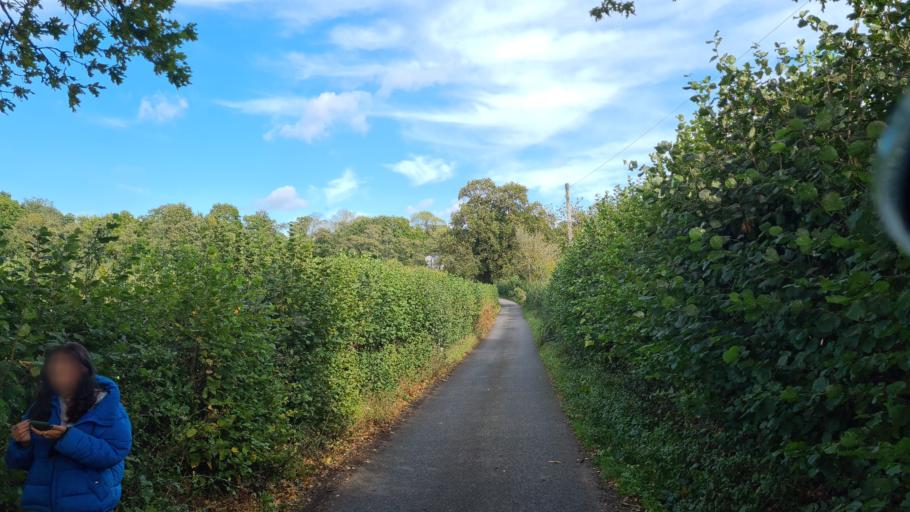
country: GB
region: England
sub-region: East Sussex
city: Battle
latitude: 50.9228
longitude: 0.5448
